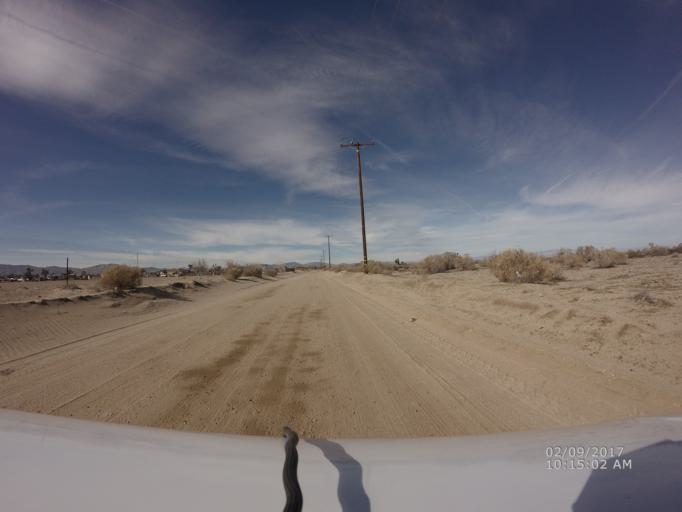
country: US
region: California
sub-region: Los Angeles County
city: Littlerock
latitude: 34.5726
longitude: -117.9104
